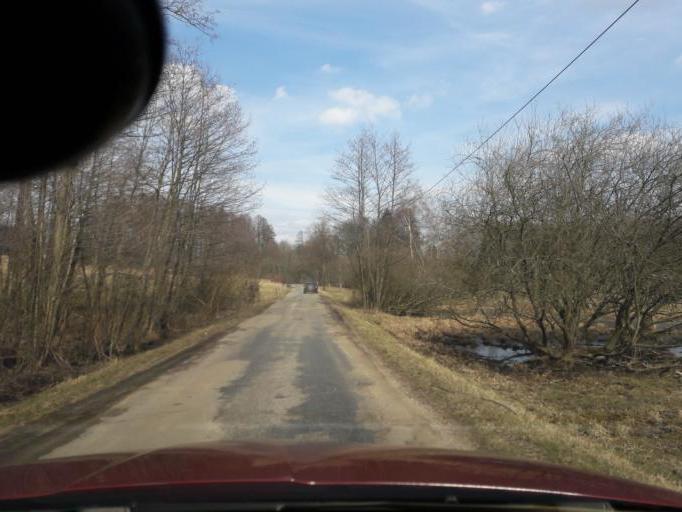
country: CZ
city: Zakupy
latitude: 50.7227
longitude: 14.6190
